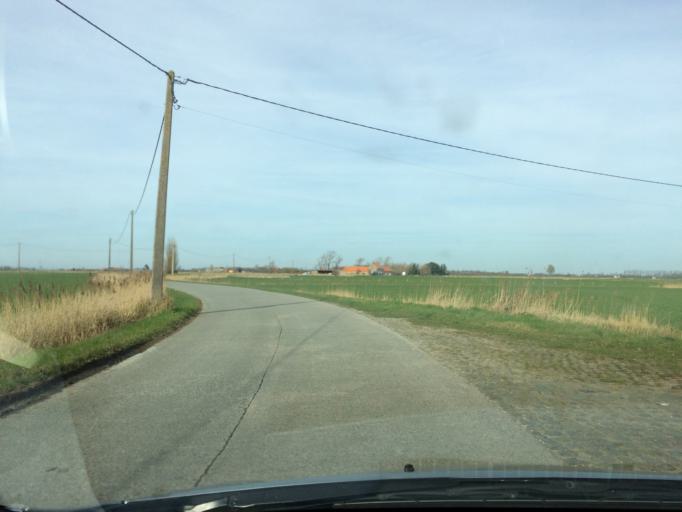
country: BE
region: Flanders
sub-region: Provincie West-Vlaanderen
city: Diksmuide
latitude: 51.0551
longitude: 2.8269
